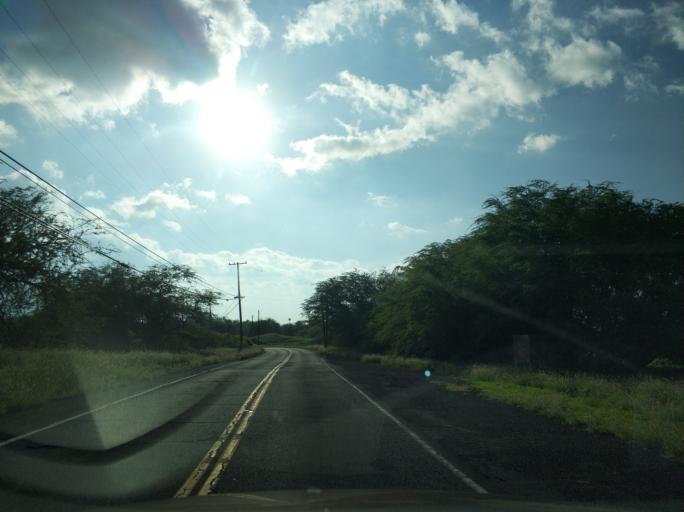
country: US
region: Hawaii
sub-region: Hawaii County
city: Waikoloa Village
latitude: 19.9741
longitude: -155.8290
